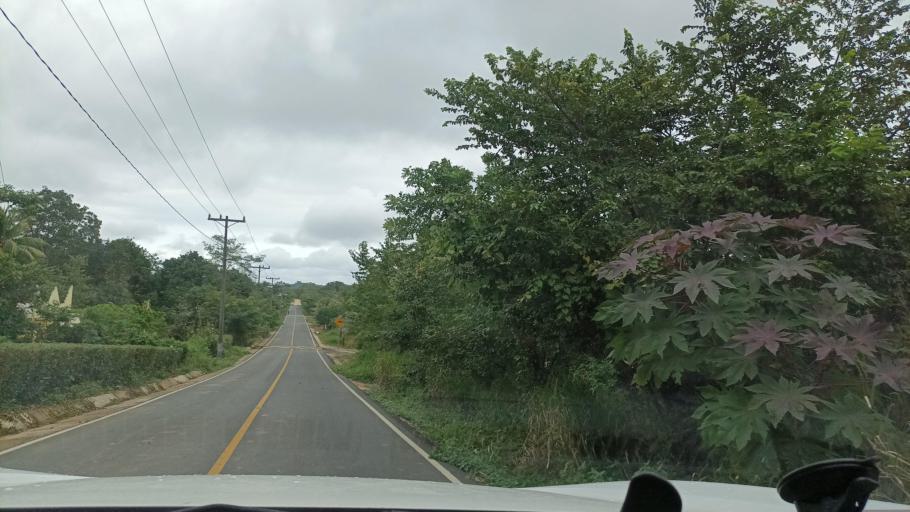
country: MX
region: Veracruz
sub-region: Moloacan
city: Cuichapa
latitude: 17.8109
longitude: -94.3558
